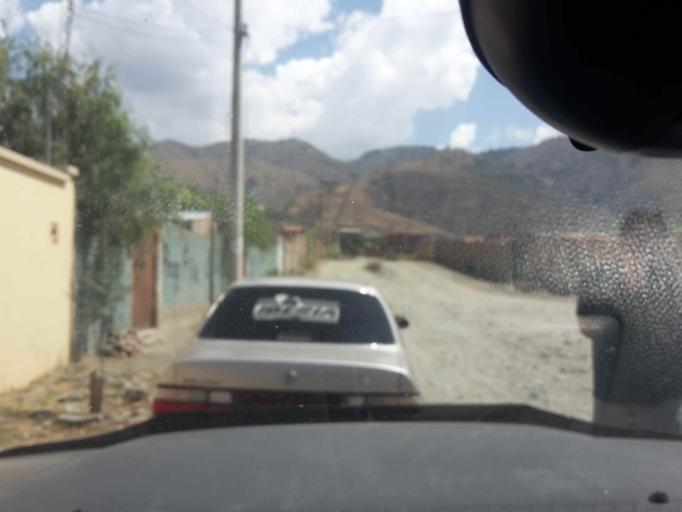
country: BO
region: Cochabamba
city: Cochabamba
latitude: -17.3836
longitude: -66.0667
